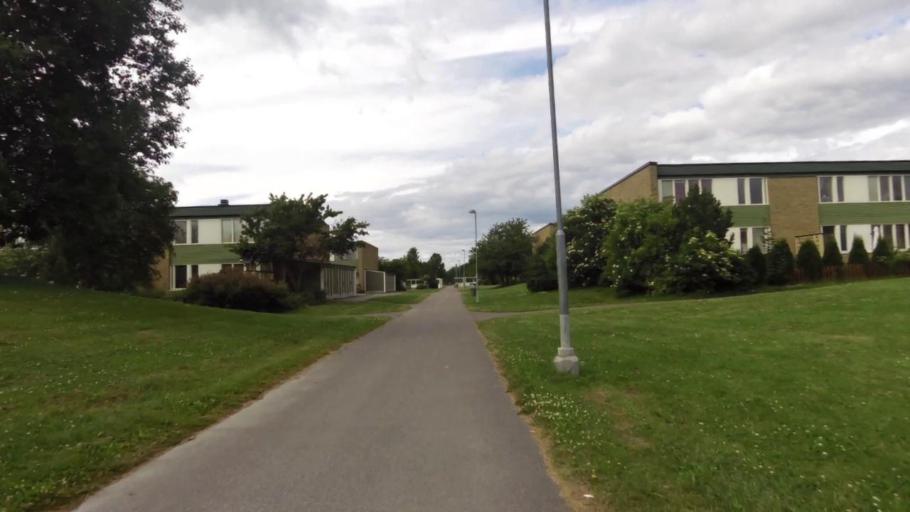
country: SE
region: OEstergoetland
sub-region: Linkopings Kommun
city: Linkoping
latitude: 58.4128
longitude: 15.5692
